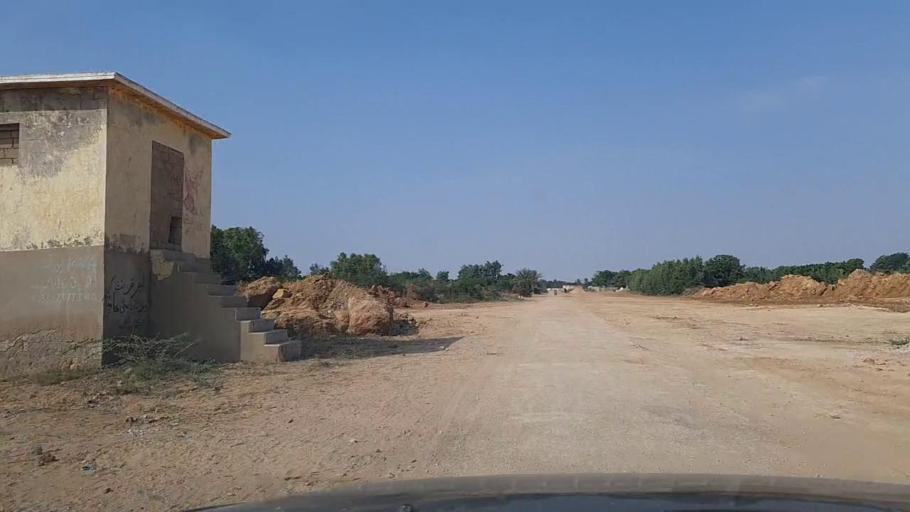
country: PK
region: Sindh
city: Gharo
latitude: 24.7625
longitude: 67.5781
